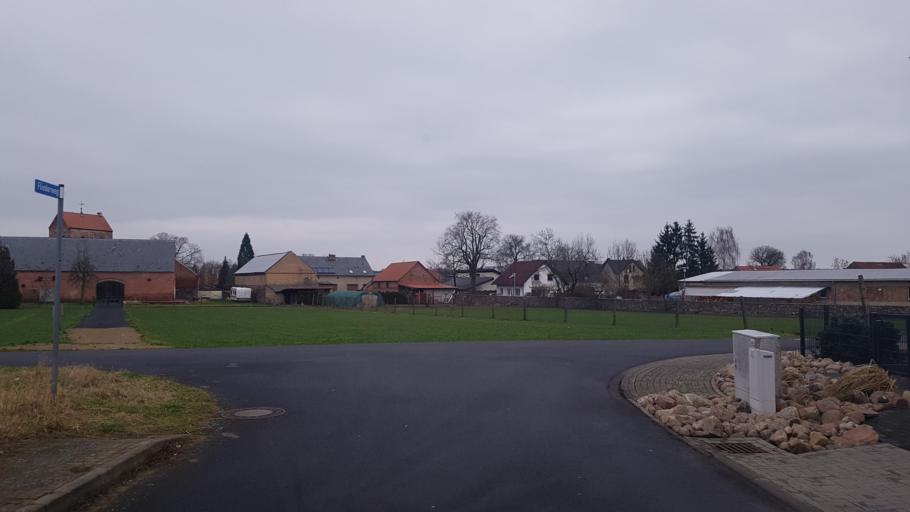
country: DE
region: Brandenburg
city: Oranienburg
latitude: 52.8723
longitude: 13.2252
